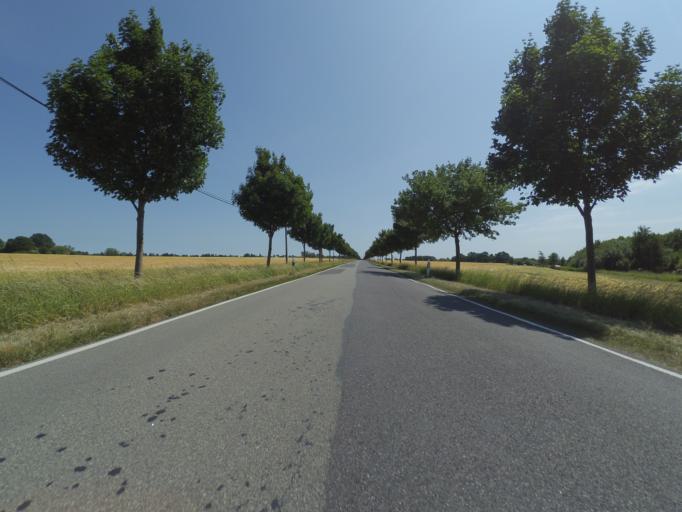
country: DE
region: Brandenburg
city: Gerdshagen
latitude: 53.3092
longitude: 12.2810
